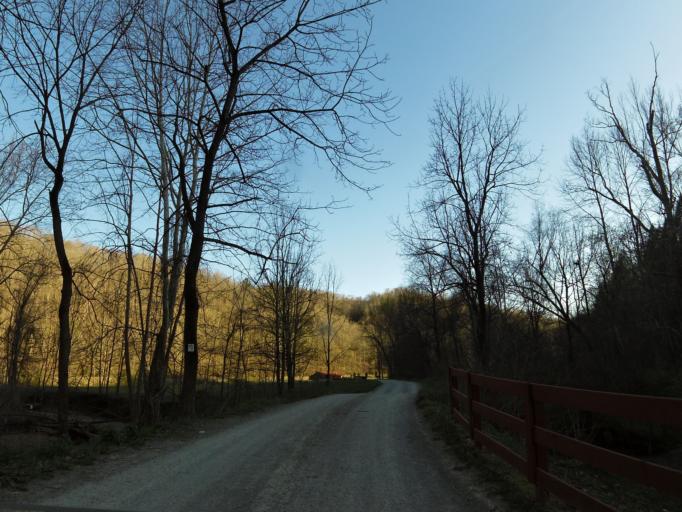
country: US
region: Tennessee
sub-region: Campbell County
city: Caryville
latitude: 36.2707
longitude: -84.3440
